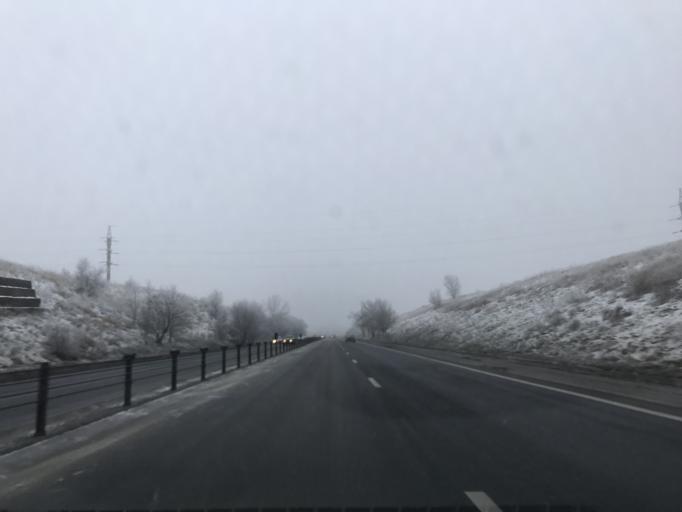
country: RU
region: Rostov
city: Grushevskaya
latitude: 47.4346
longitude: 39.9750
